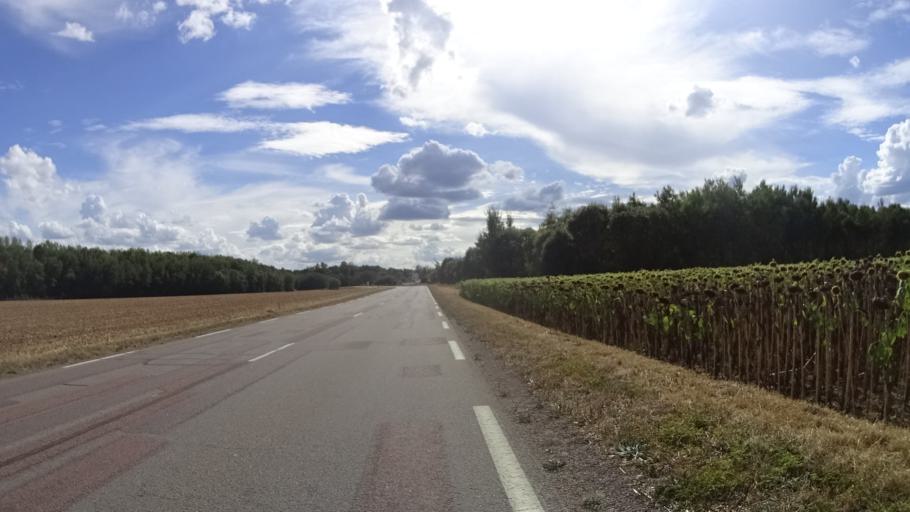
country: FR
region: Bourgogne
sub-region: Departement de la Cote-d'Or
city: Seurre
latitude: 47.0381
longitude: 5.1832
